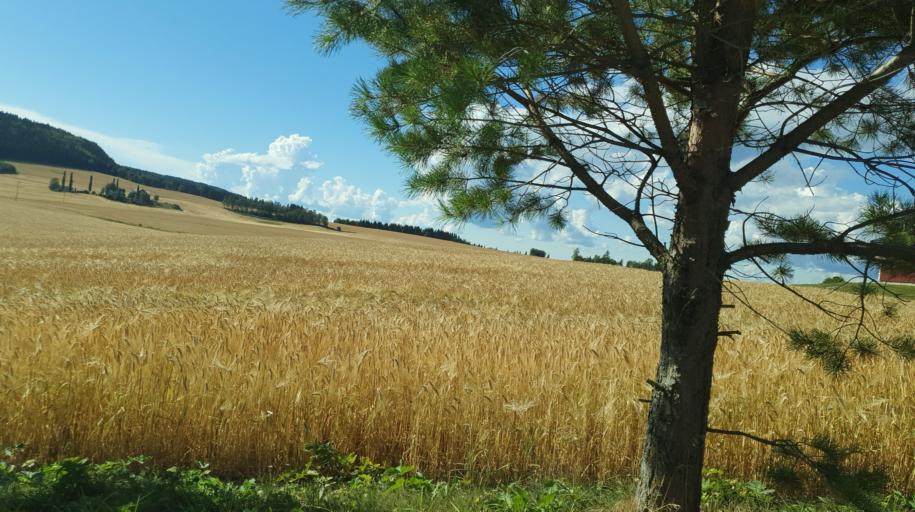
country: NO
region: Nord-Trondelag
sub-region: Verdal
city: Verdal
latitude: 63.7763
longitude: 11.3977
